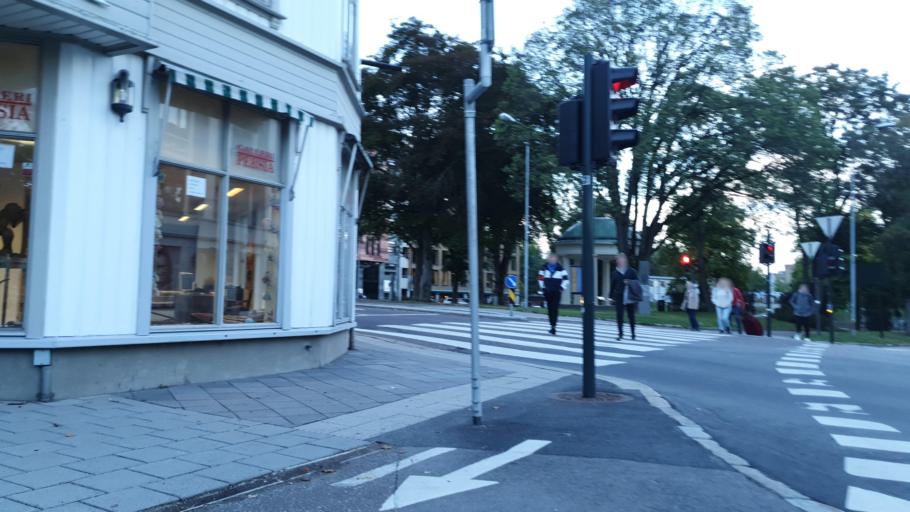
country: NO
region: Vestfold
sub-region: Tonsberg
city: Tonsberg
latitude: 59.2701
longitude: 10.4095
